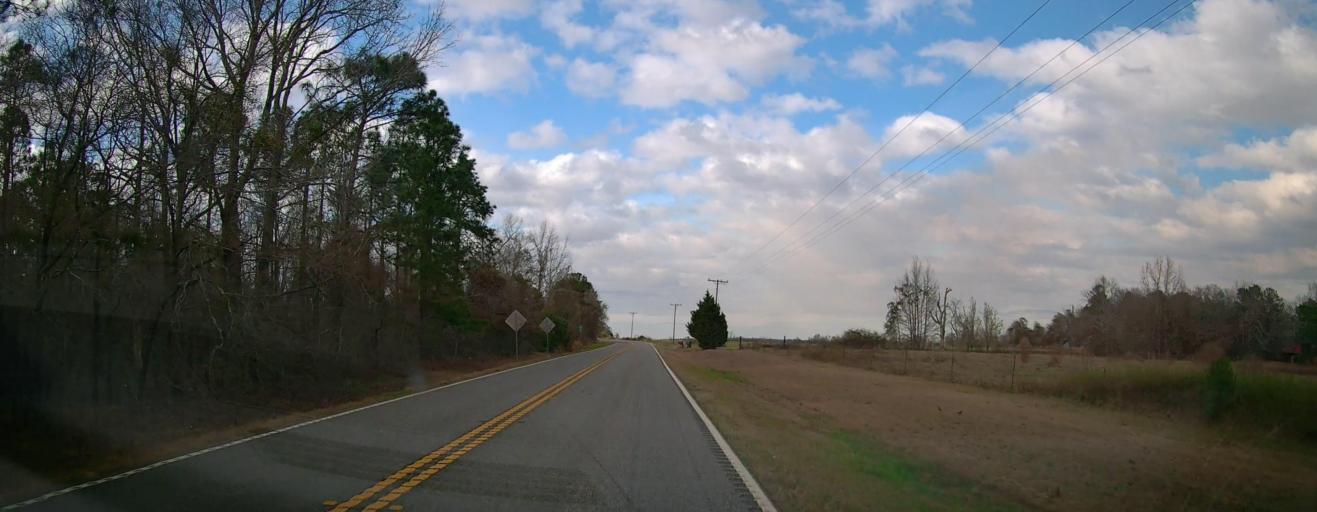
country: US
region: Georgia
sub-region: Marion County
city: Buena Vista
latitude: 32.4456
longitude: -84.4405
